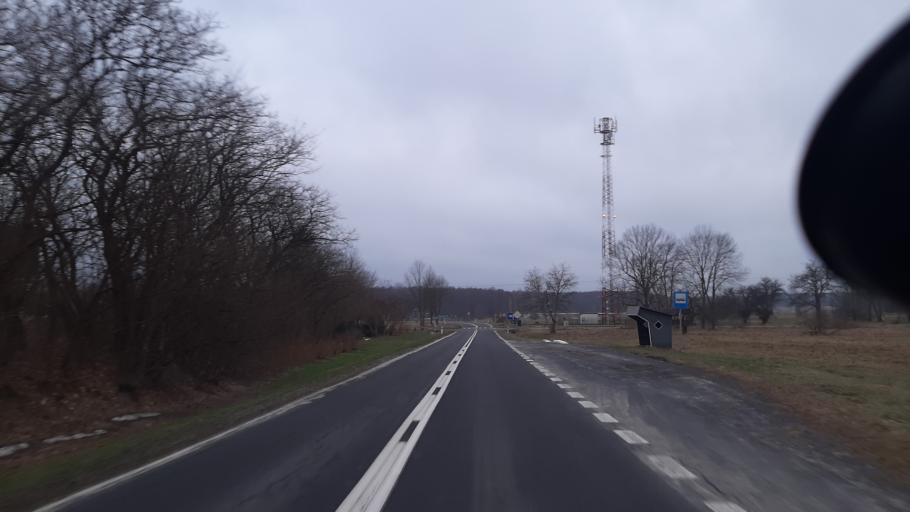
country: PL
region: Lublin Voivodeship
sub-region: Powiat parczewski
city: Podedworze
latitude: 51.5589
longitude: 23.3107
